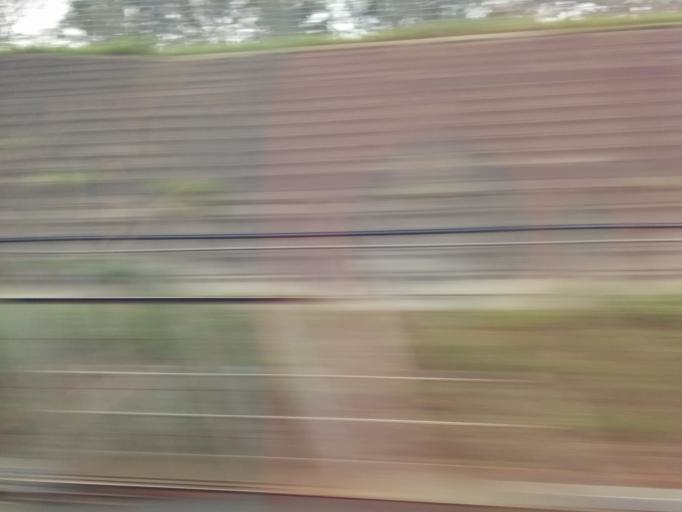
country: JP
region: Kanagawa
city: Yokohama
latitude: 35.4828
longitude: 139.5802
